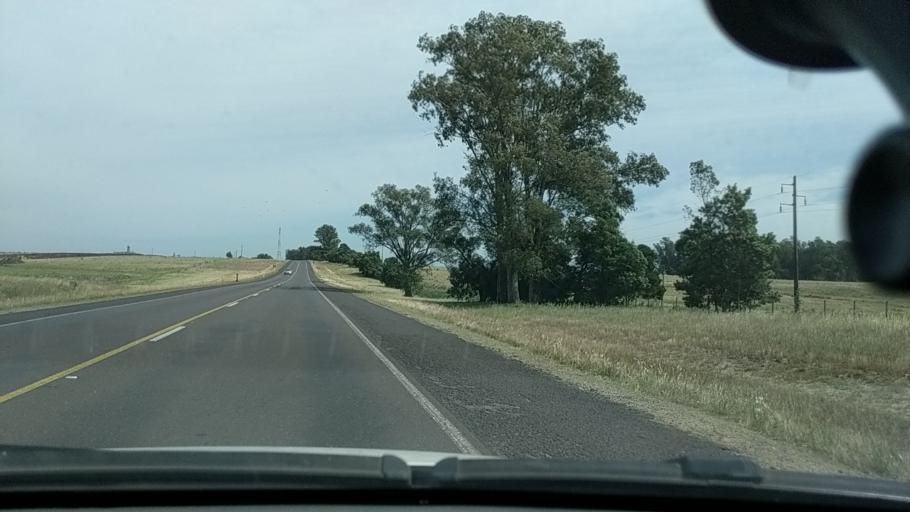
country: UY
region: Durazno
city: Durazno
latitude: -33.5070
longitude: -56.4173
